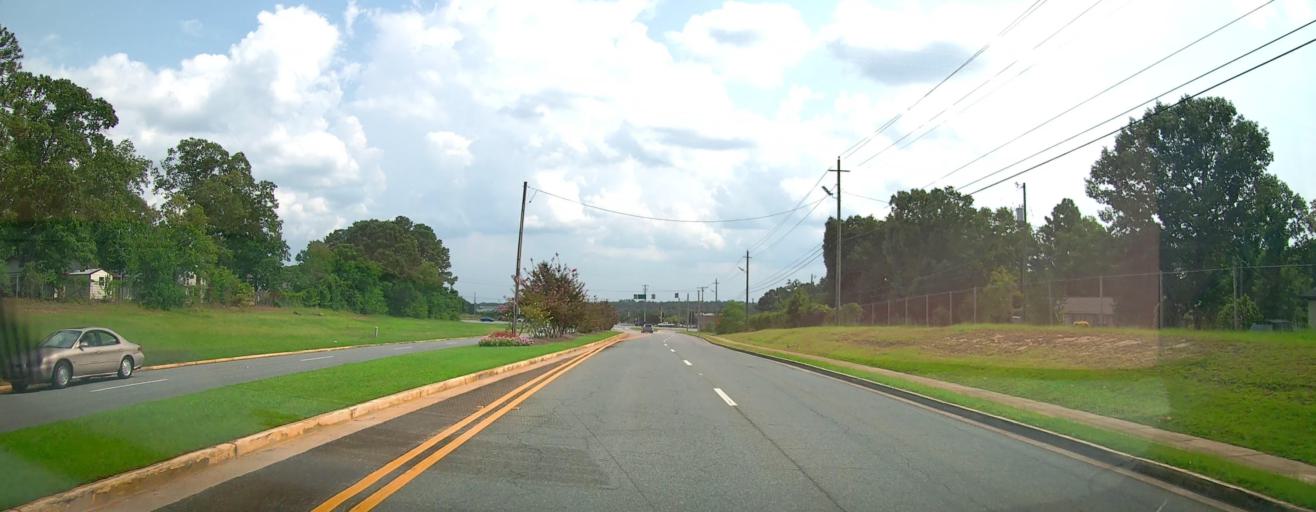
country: US
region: Georgia
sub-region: Houston County
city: Warner Robins
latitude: 32.5959
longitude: -83.6137
